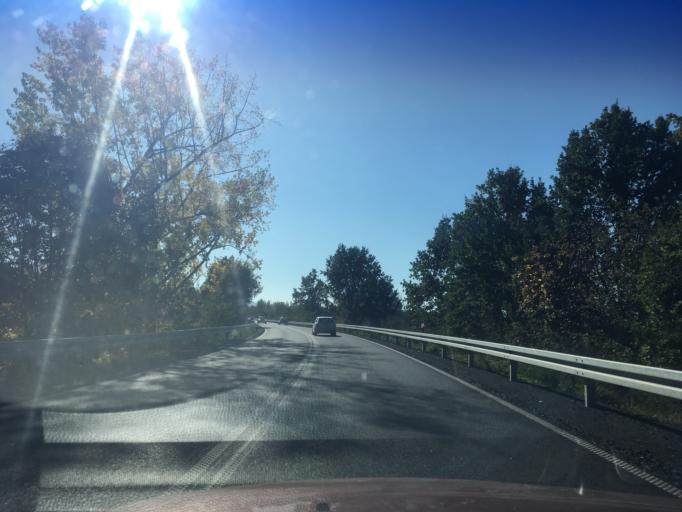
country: DE
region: Saxony
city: Hirschfelde
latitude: 50.9249
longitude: 14.8729
